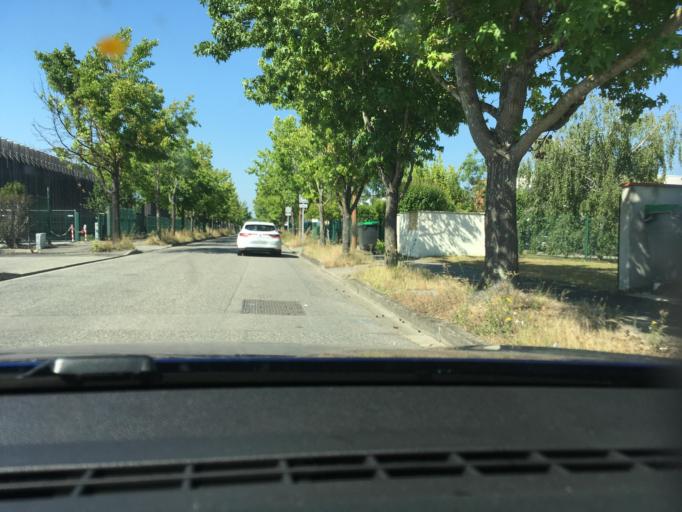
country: FR
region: Midi-Pyrenees
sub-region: Departement de la Haute-Garonne
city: Portet-sur-Garonne
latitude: 43.5674
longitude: 1.3848
